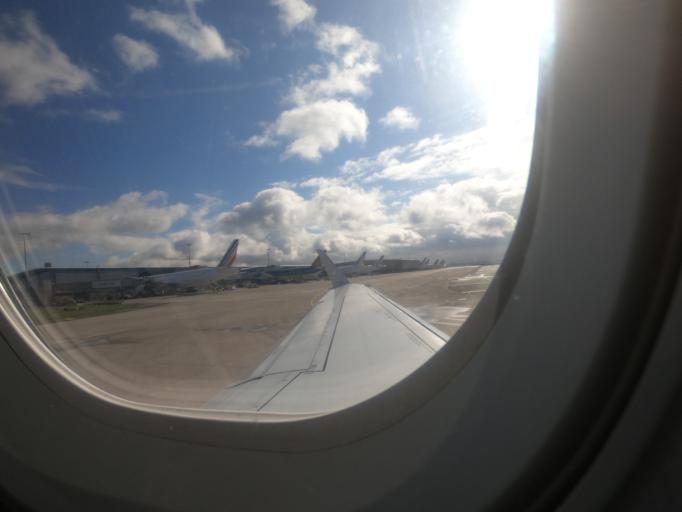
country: FR
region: Ile-de-France
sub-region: Departement de Seine-et-Marne
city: Mitry-Mory
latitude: 49.0086
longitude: 2.5875
